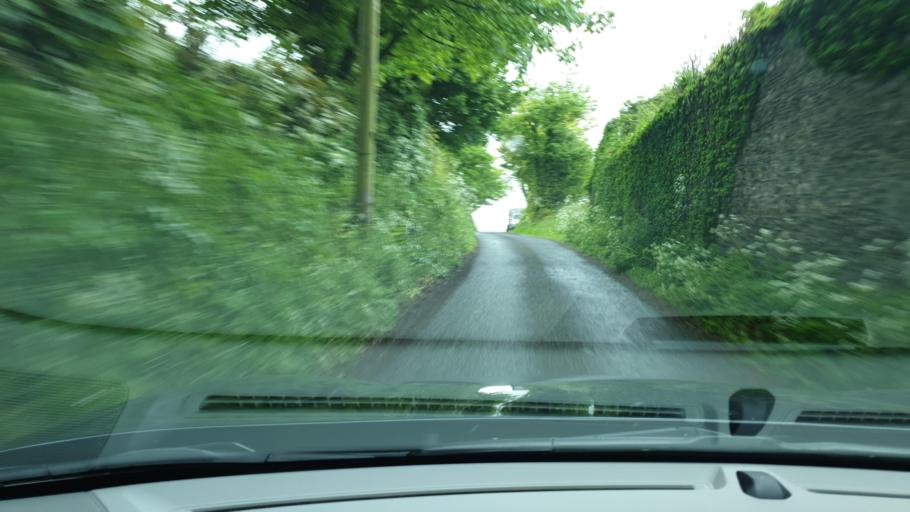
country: IE
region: Leinster
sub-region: Laois
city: Portlaoise
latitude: 53.0367
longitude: -7.3381
